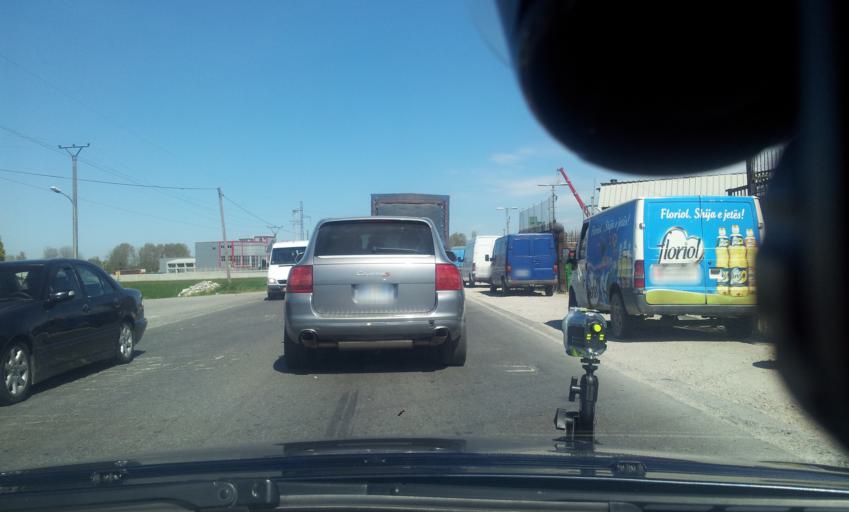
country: AL
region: Durres
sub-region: Rrethi i Krujes
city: Hasan
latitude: 41.4842
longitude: 19.7088
